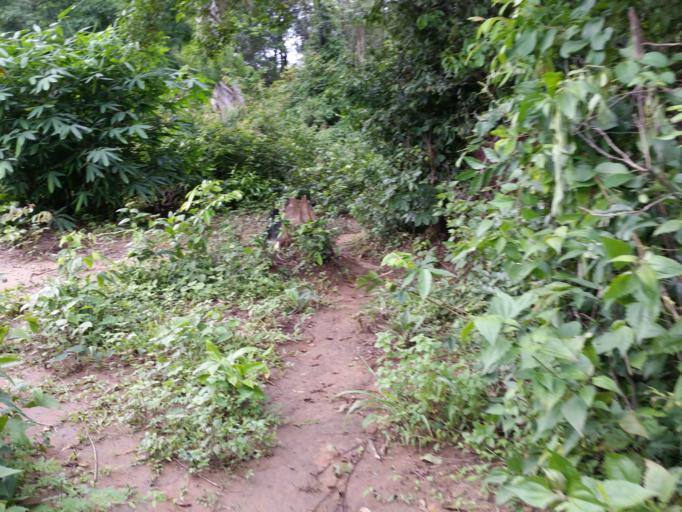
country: LA
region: Xekong
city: Thateng
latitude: 15.5262
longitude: 106.2726
